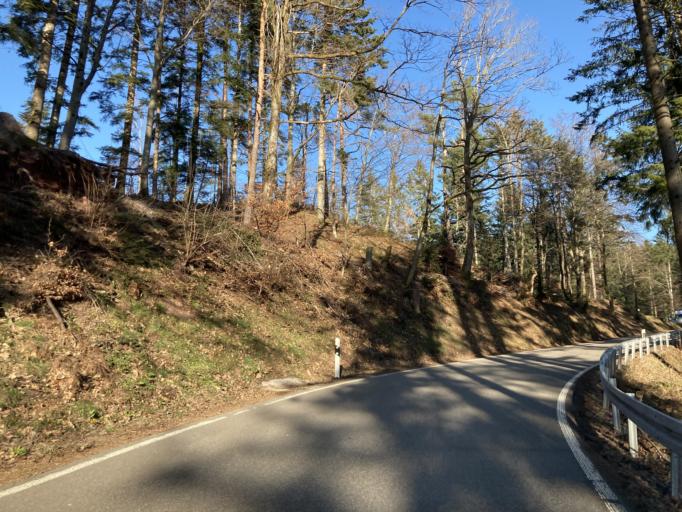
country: DE
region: Baden-Wuerttemberg
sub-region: Freiburg Region
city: Oppenau
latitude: 48.4865
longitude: 8.2107
